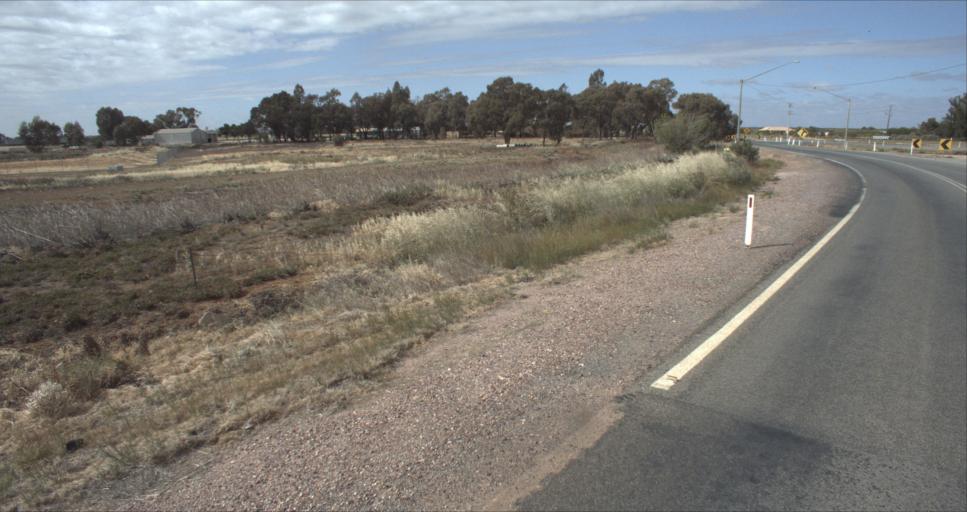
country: AU
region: New South Wales
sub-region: Leeton
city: Leeton
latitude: -34.5684
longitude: 146.3951
